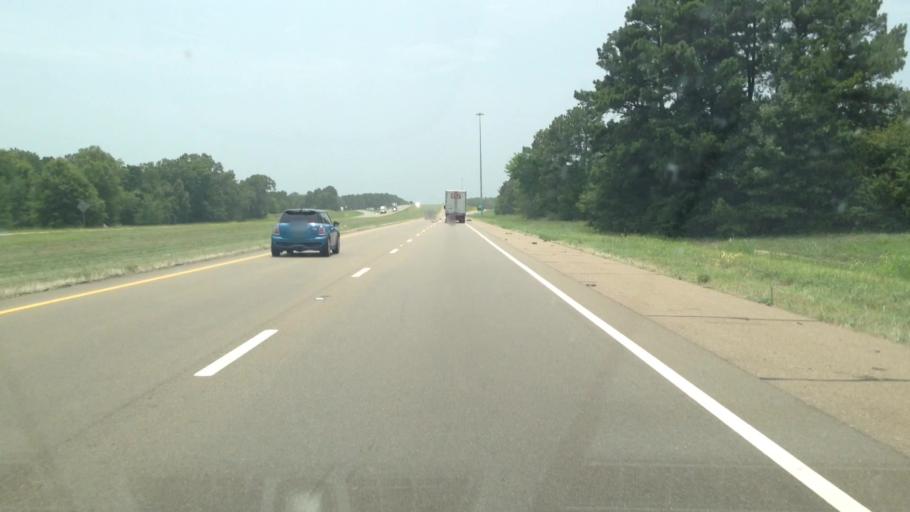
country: US
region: Texas
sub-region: Bowie County
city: De Kalb
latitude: 33.4215
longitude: -94.5503
